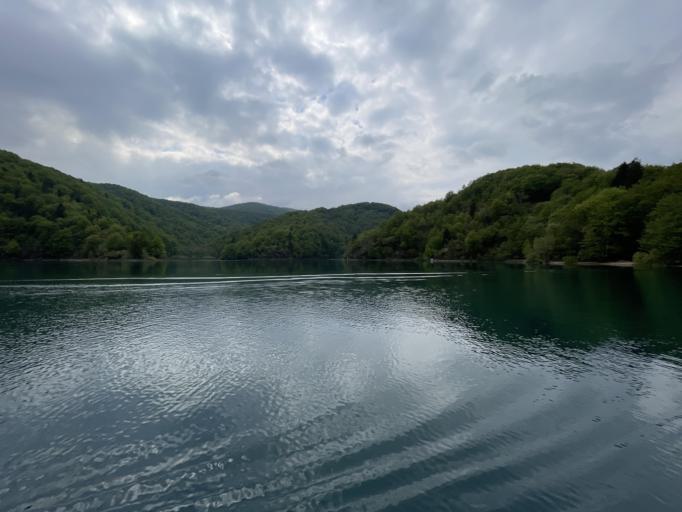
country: HR
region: Licko-Senjska
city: Jezerce
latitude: 44.8928
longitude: 15.6042
